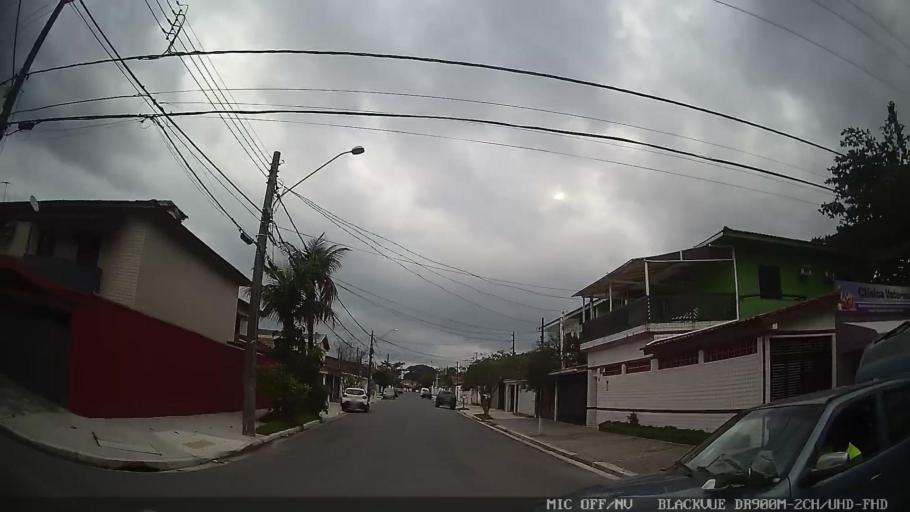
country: BR
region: Sao Paulo
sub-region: Guaruja
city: Guaruja
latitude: -23.9943
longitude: -46.2813
